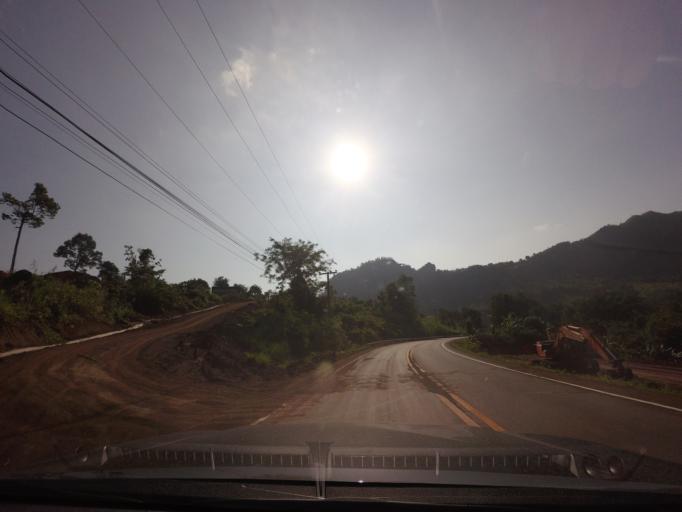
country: TH
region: Phetchabun
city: Lom Kao
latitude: 16.8686
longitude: 101.1386
